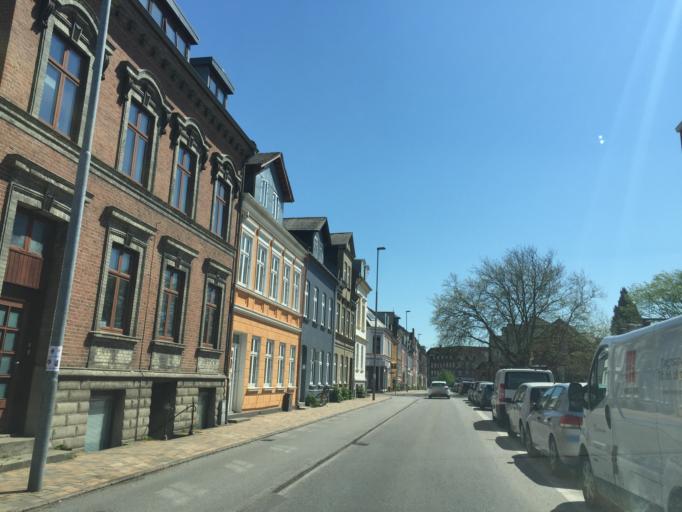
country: DK
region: South Denmark
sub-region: Odense Kommune
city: Odense
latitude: 55.3924
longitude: 10.3905
